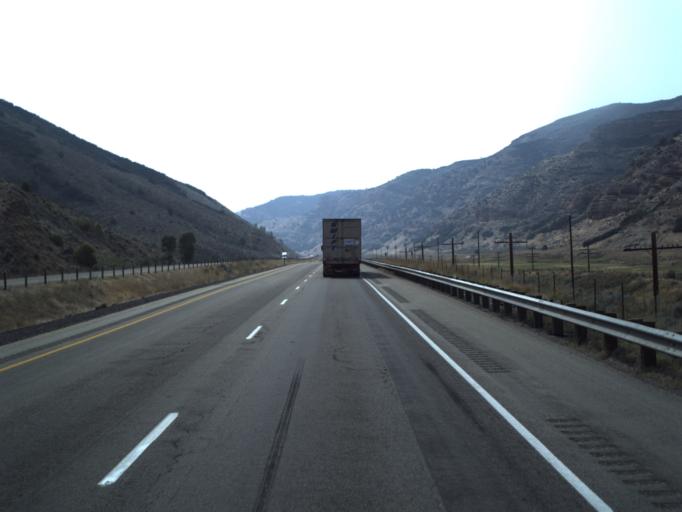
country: US
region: Utah
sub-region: Summit County
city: Coalville
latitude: 41.0267
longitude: -111.3469
